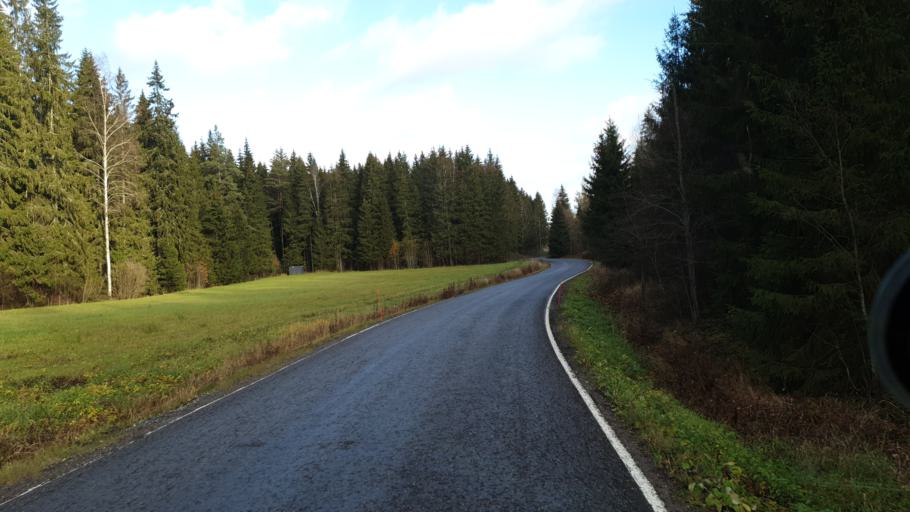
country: FI
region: Uusimaa
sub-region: Helsinki
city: Siuntio
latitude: 60.2621
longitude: 24.3019
